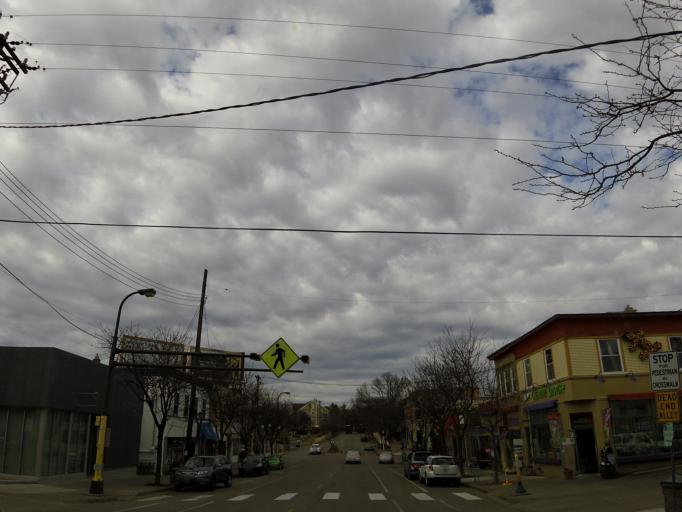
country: US
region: Minnesota
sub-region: Hennepin County
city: Saint Louis Park
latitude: 44.9238
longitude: -93.3149
